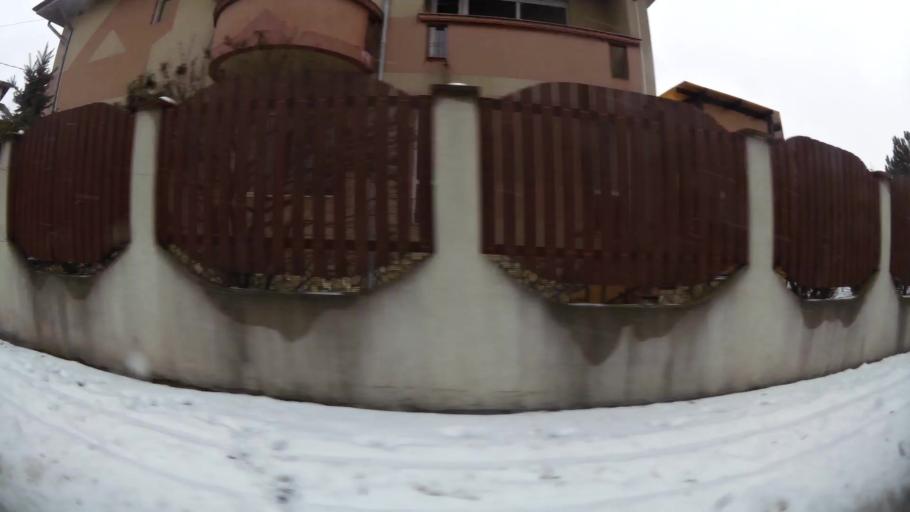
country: RO
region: Ilfov
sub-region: Comuna Mogosoaia
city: Mogosoaia
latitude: 44.5077
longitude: 26.0161
